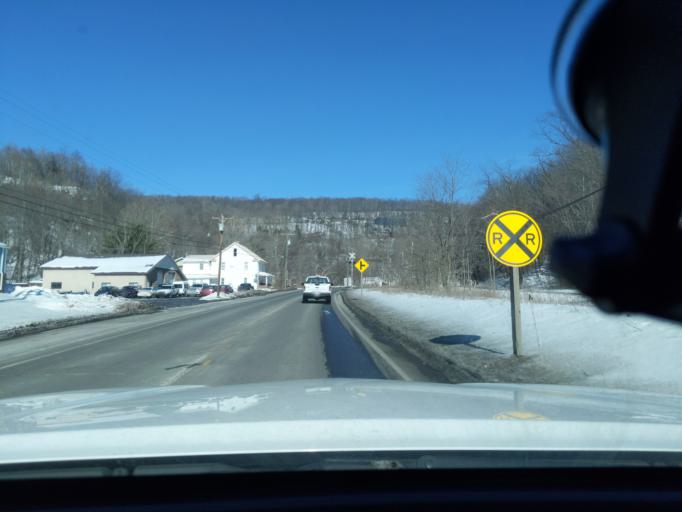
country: US
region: Maryland
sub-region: Allegany County
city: Lonaconing
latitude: 39.5776
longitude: -78.9726
